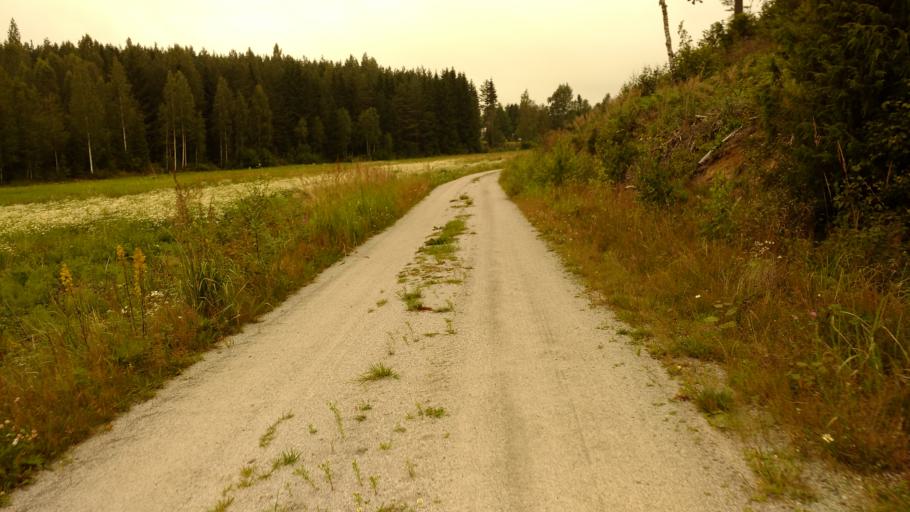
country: FI
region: Varsinais-Suomi
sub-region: Salo
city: Pertteli
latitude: 60.4049
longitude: 23.2275
